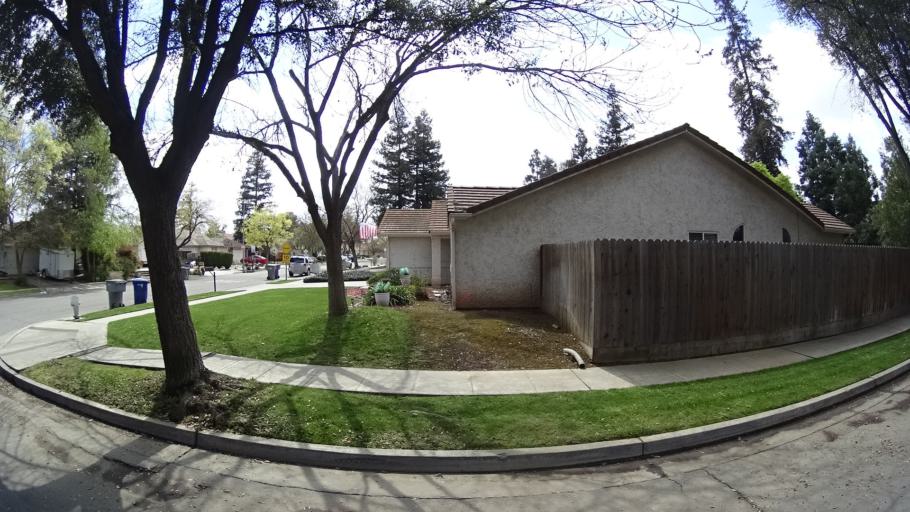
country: US
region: California
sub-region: Fresno County
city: Fresno
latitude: 36.8263
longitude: -119.8495
